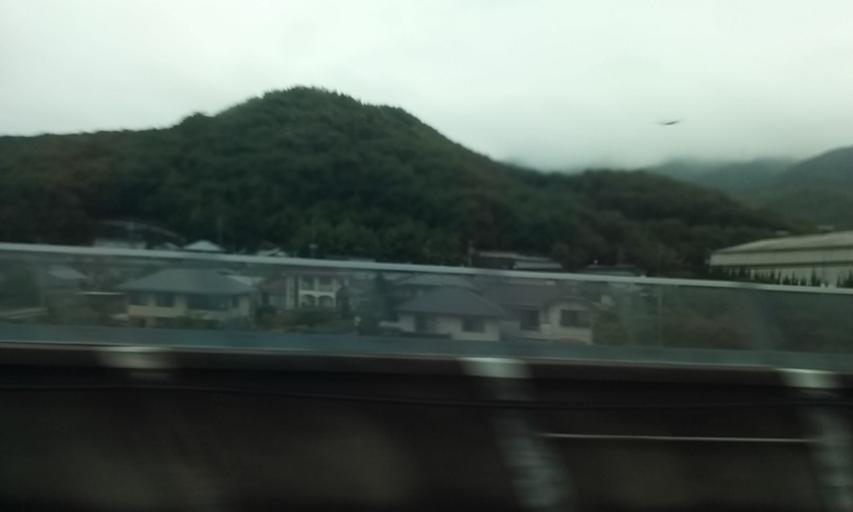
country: JP
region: Okayama
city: Okayama-shi
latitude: 34.7275
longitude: 134.1125
